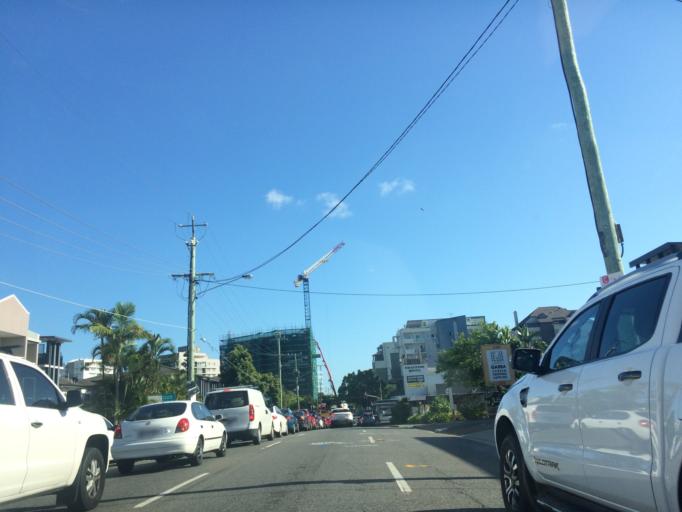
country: AU
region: Queensland
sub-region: Brisbane
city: Woolloongabba
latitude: -27.4802
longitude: 153.0412
